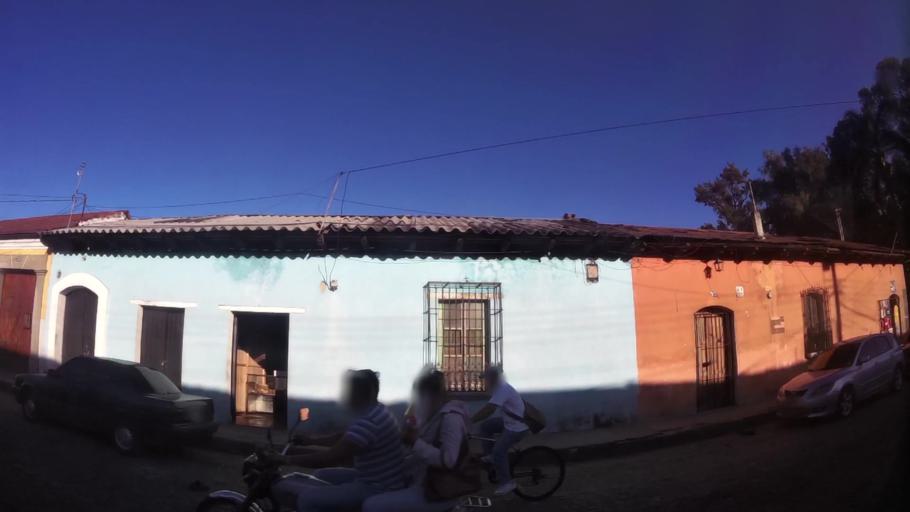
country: GT
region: Sacatepequez
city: Antigua Guatemala
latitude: 14.5648
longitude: -90.7373
